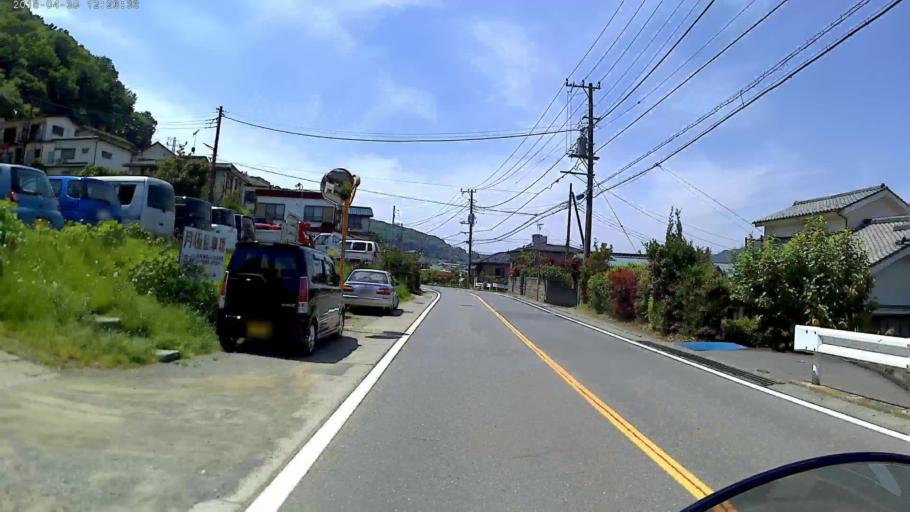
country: JP
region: Tokyo
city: Hachioji
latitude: 35.5824
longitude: 139.2651
